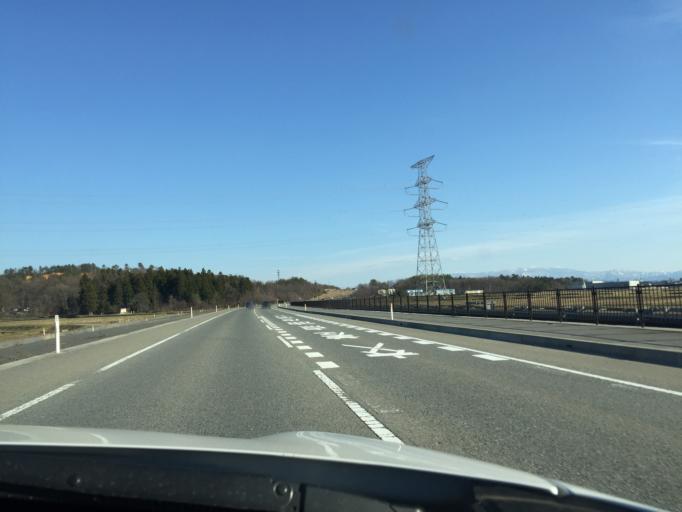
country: JP
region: Yamagata
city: Nagai
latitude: 38.0693
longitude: 140.0486
